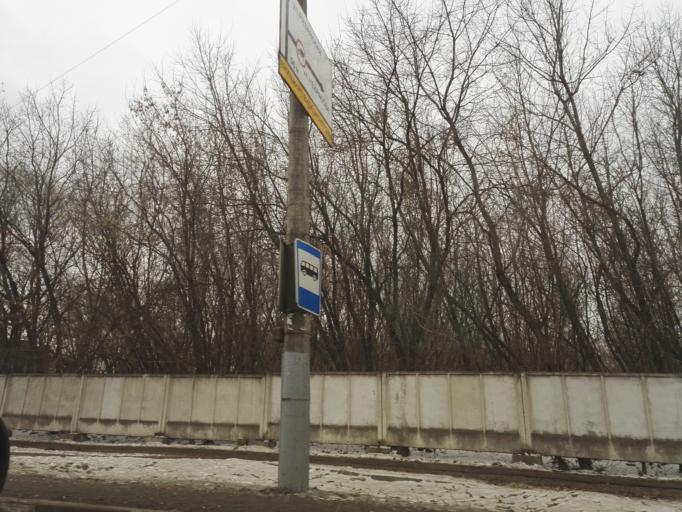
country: RU
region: Tula
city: Tula
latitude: 54.1743
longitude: 37.6334
